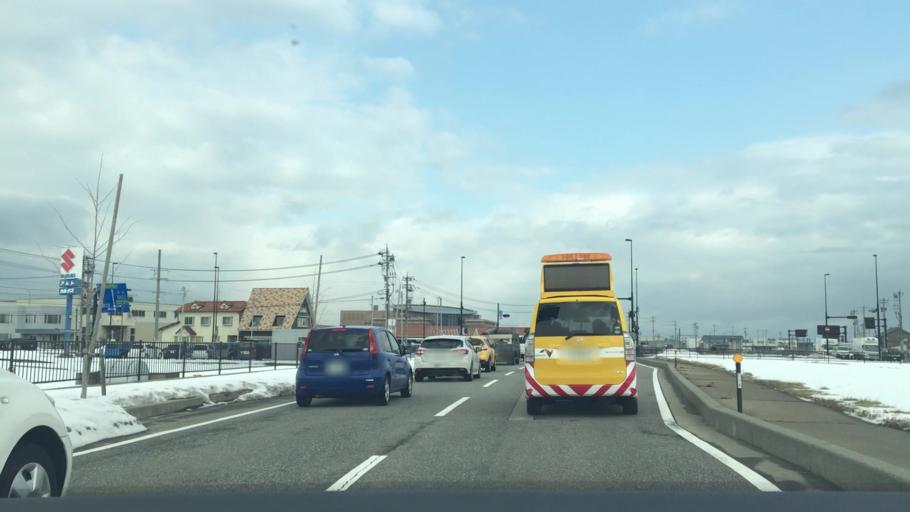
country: JP
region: Ishikawa
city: Matsuto
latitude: 36.5565
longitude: 136.5794
